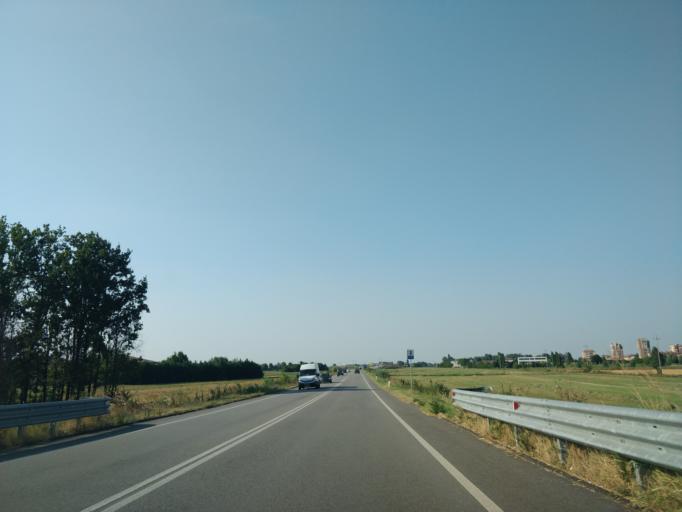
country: IT
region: Emilia-Romagna
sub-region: Provincia di Bologna
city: Castel Maggiore
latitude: 44.5700
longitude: 11.3461
